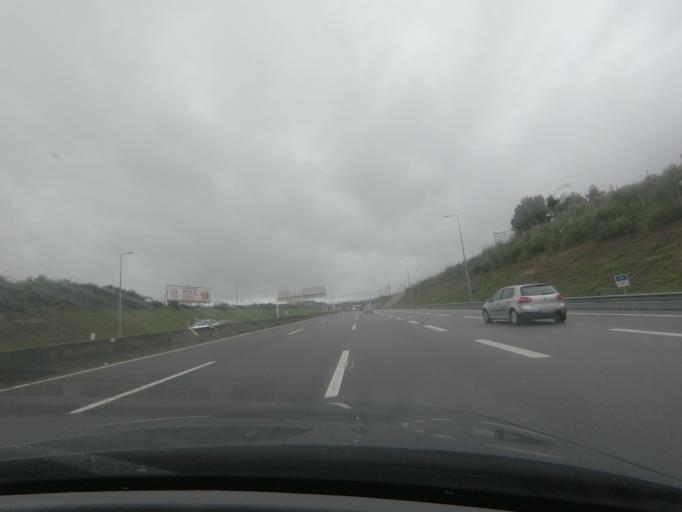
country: PT
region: Porto
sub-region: Matosinhos
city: Santa Cruz do Bispo
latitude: 41.2273
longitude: -8.6729
